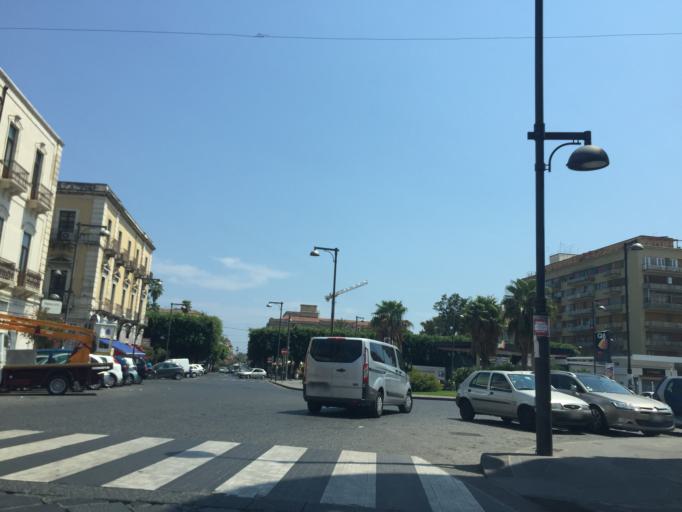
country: IT
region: Sicily
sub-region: Provincia di Siracusa
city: Siracusa
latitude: 37.0668
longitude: 15.2835
